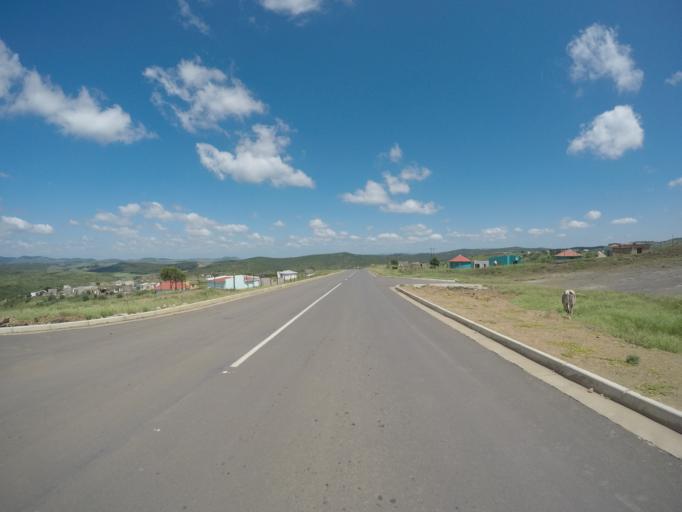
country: ZA
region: KwaZulu-Natal
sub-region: uThungulu District Municipality
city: Empangeni
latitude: -28.6078
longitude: 31.7466
